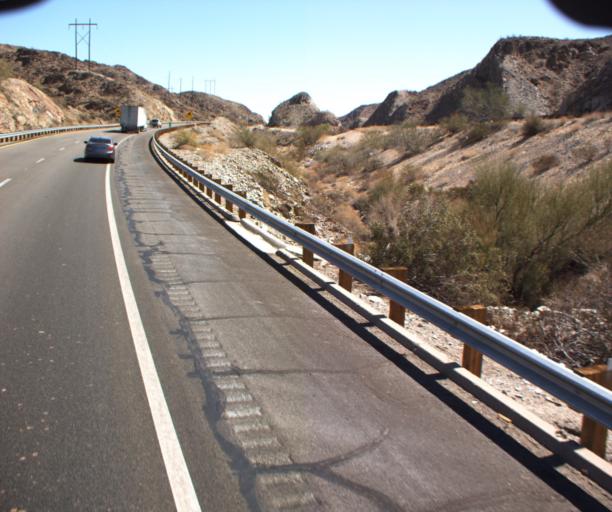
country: US
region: Arizona
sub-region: Yuma County
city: Fortuna Foothills
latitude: 32.6603
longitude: -114.3323
